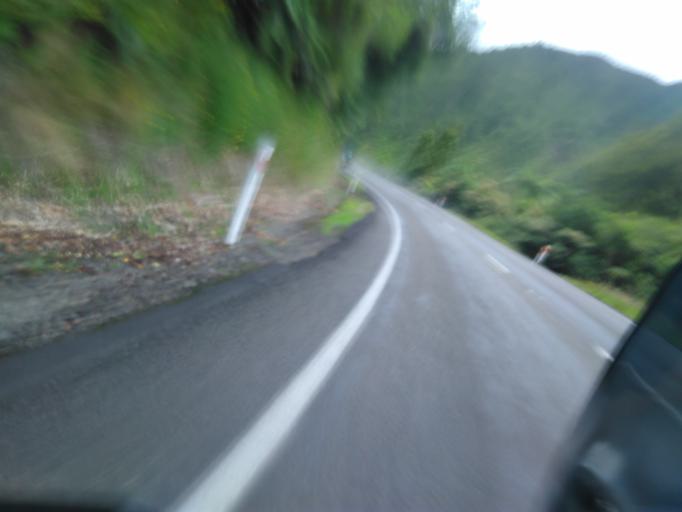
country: NZ
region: Bay of Plenty
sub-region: Opotiki District
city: Opotiki
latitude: -38.2368
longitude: 177.3084
